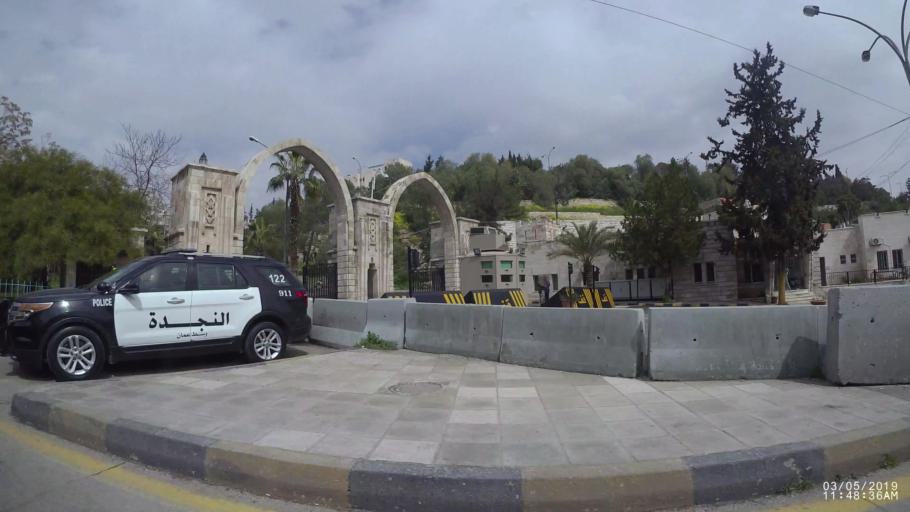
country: JO
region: Amman
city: Amman
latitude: 31.9548
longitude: 35.9442
